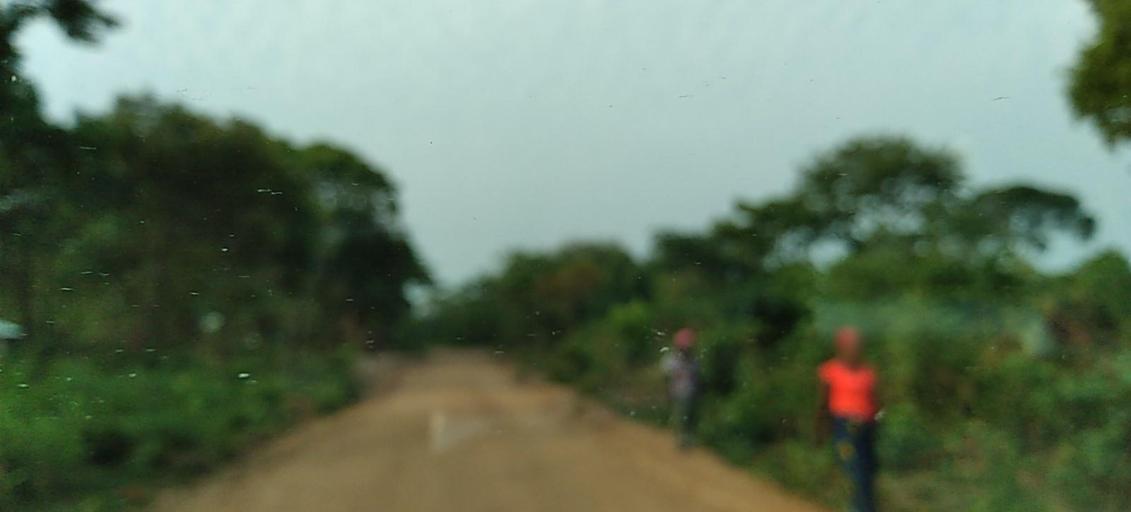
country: ZM
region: Copperbelt
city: Kalulushi
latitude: -12.8882
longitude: 27.6895
